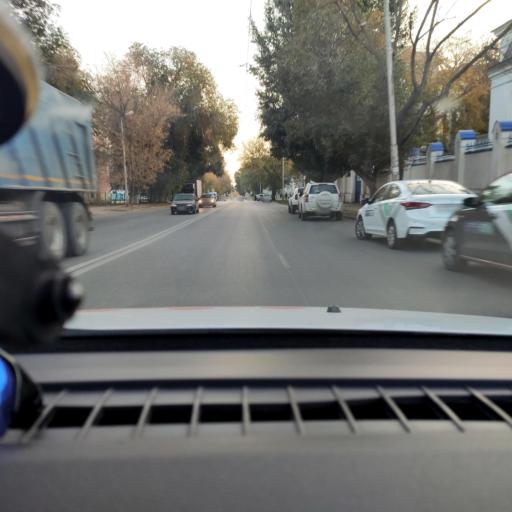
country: RU
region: Samara
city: Samara
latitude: 53.1863
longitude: 50.1086
